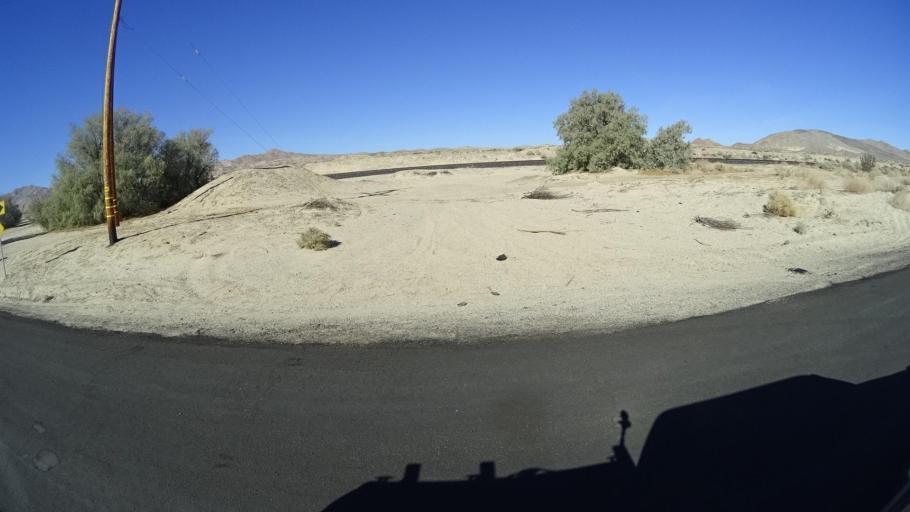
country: US
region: California
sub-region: Kern County
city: California City
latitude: 35.3090
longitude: -117.9680
